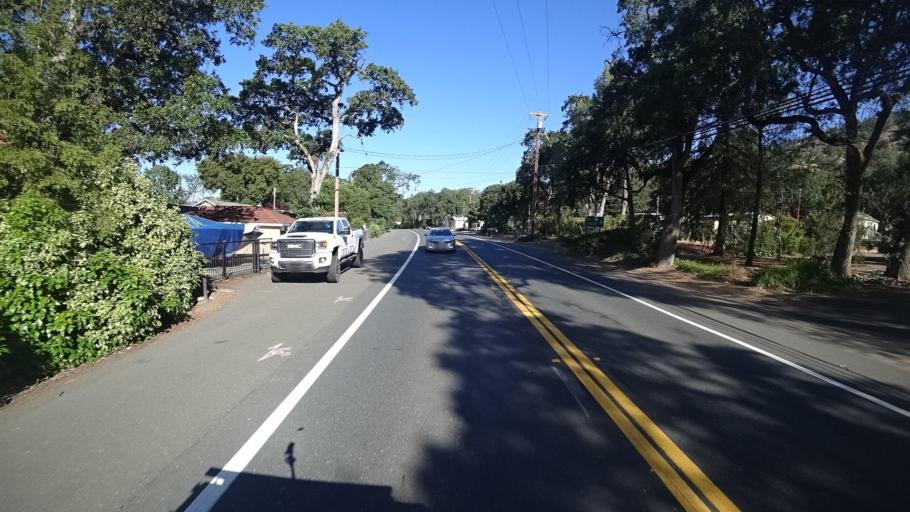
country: US
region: California
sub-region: Lake County
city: Clearlake Oaks
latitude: 39.0214
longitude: -122.7117
